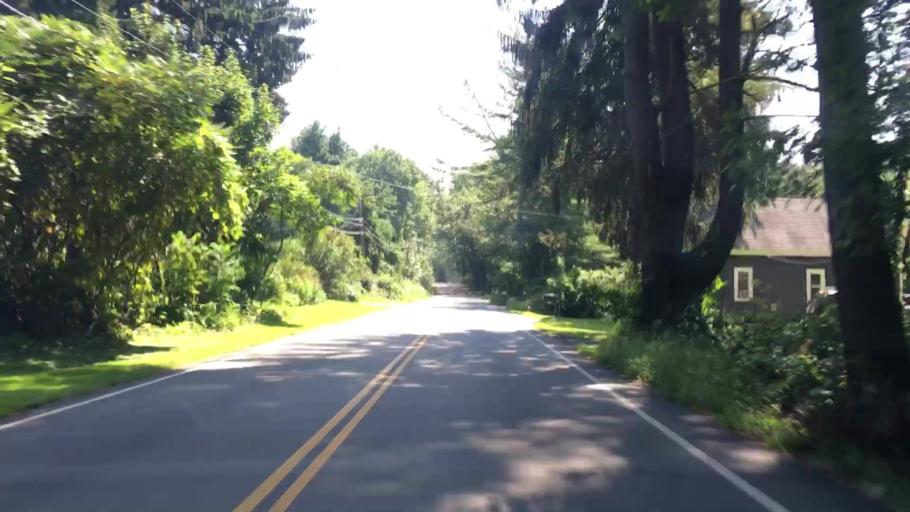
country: US
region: New Hampshire
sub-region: Rockingham County
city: Hampstead
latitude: 42.8599
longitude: -71.2225
